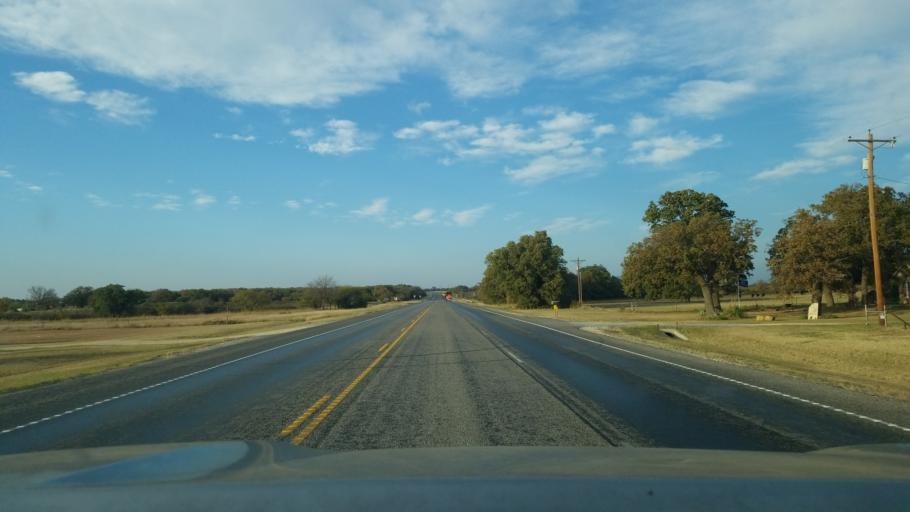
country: US
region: Texas
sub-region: Brown County
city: Lake Brownwood
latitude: 31.9990
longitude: -98.9210
